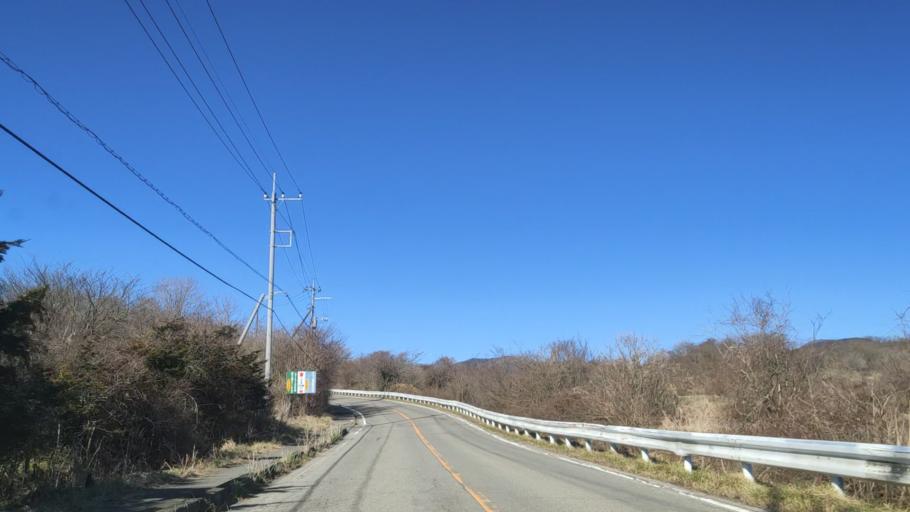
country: JP
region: Yamanashi
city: Fujikawaguchiko
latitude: 35.4088
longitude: 138.6173
